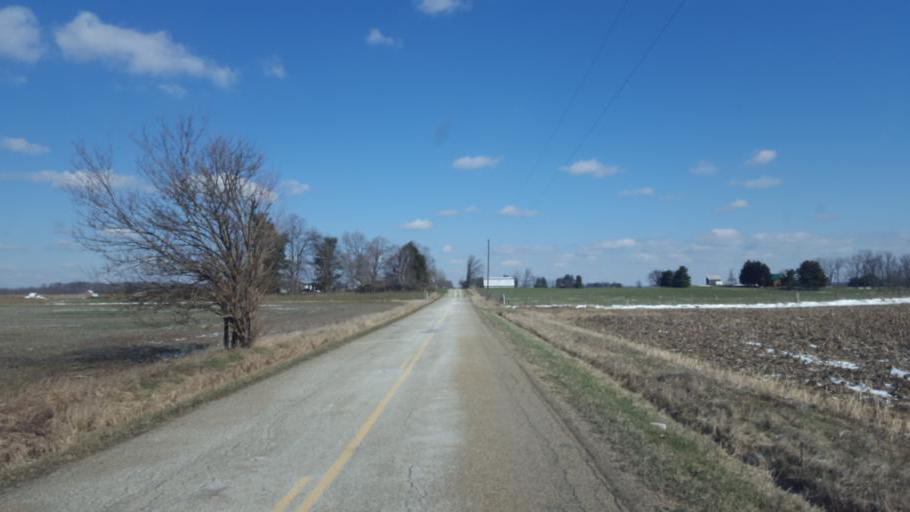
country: US
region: Ohio
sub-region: Licking County
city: Utica
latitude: 40.2818
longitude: -82.4901
